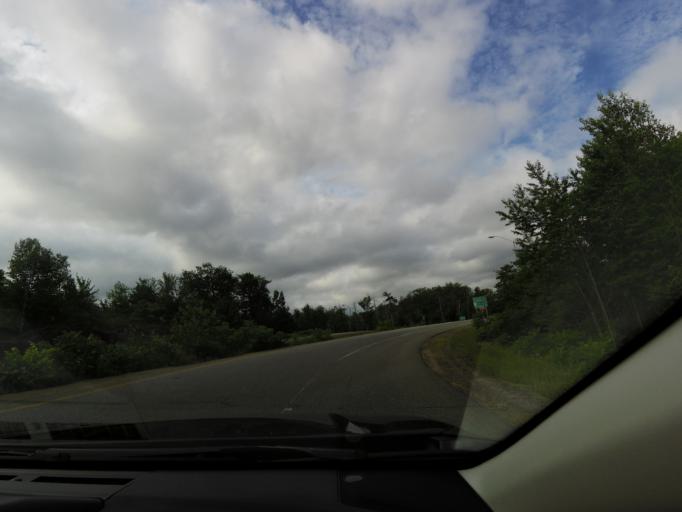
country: CA
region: Ontario
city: Bracebridge
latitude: 45.0117
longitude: -79.2950
